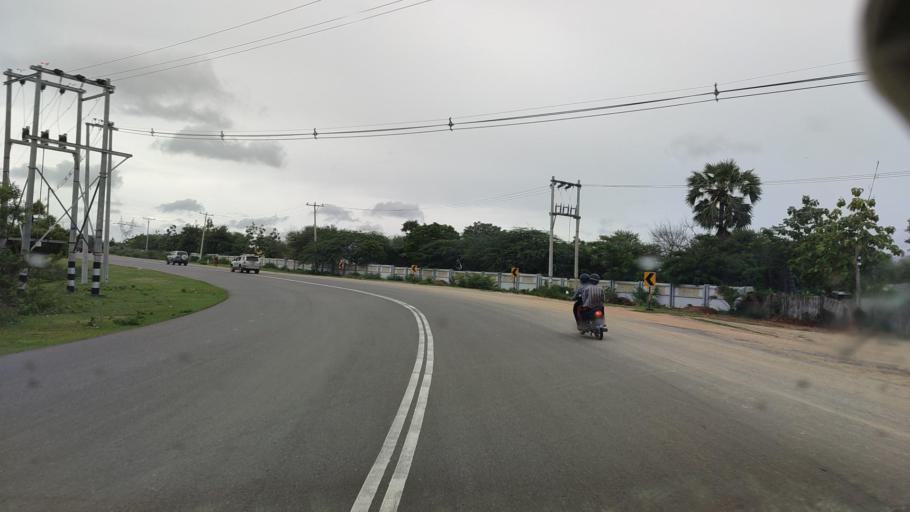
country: MM
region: Mandalay
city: Meiktila
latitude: 20.8316
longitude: 95.9006
